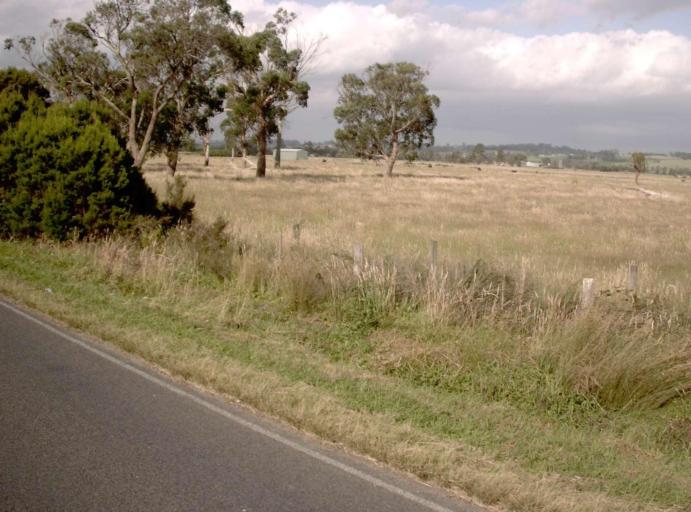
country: AU
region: Victoria
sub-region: Cardinia
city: Bunyip
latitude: -38.1333
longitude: 145.7523
